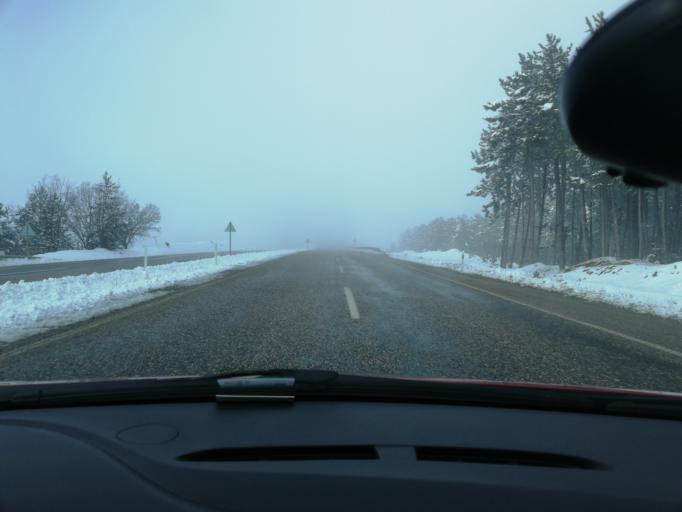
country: TR
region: Kastamonu
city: Akkaya
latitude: 41.2942
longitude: 33.4817
